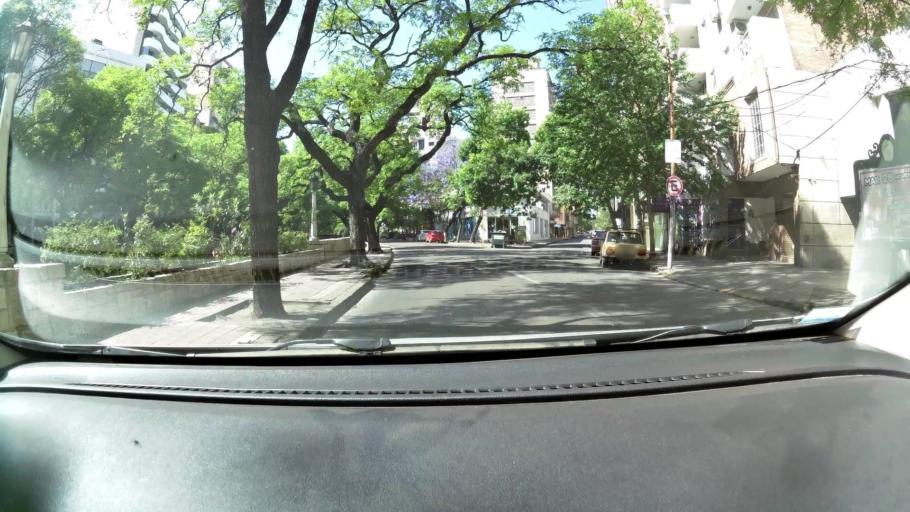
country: AR
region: Cordoba
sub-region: Departamento de Capital
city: Cordoba
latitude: -31.4127
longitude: -64.1918
